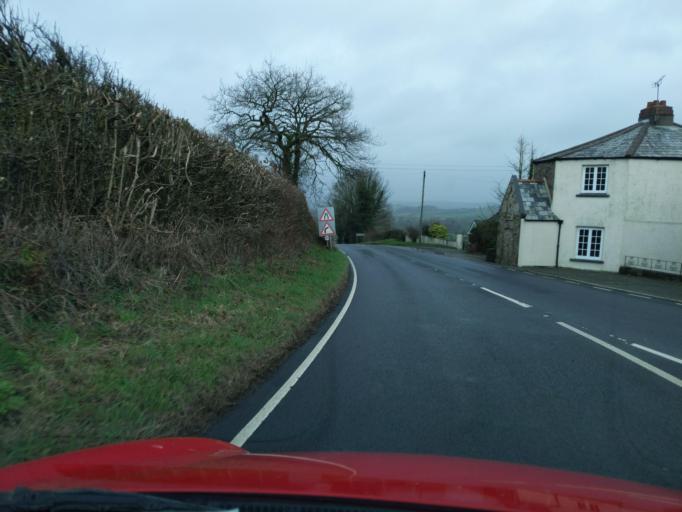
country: GB
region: England
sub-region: Cornwall
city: Launceston
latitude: 50.6476
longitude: -4.3494
